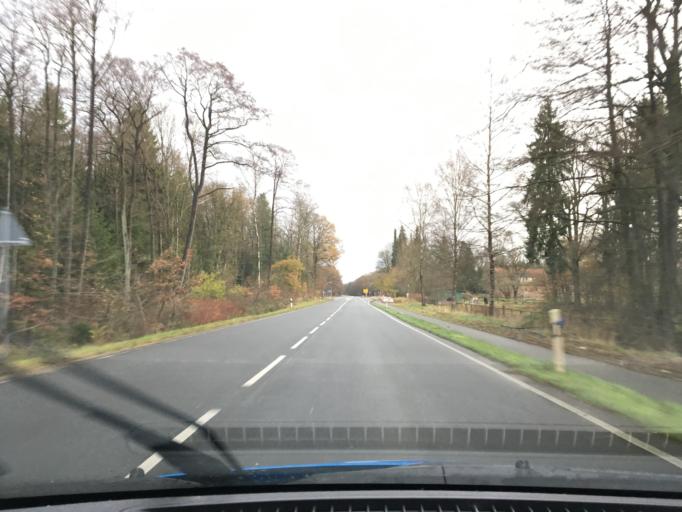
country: DE
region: Lower Saxony
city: Munster
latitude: 52.9551
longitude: 10.1227
